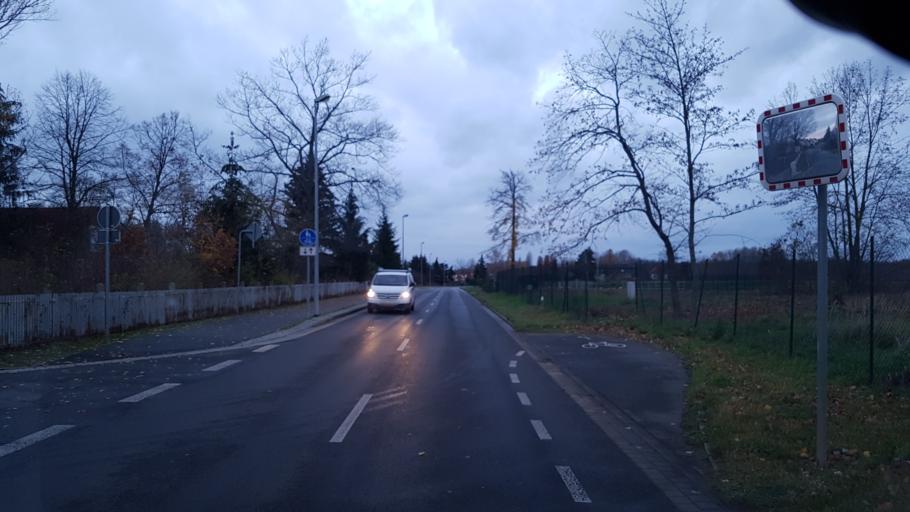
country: DE
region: Brandenburg
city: Lauchhammer
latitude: 51.4800
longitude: 13.7338
